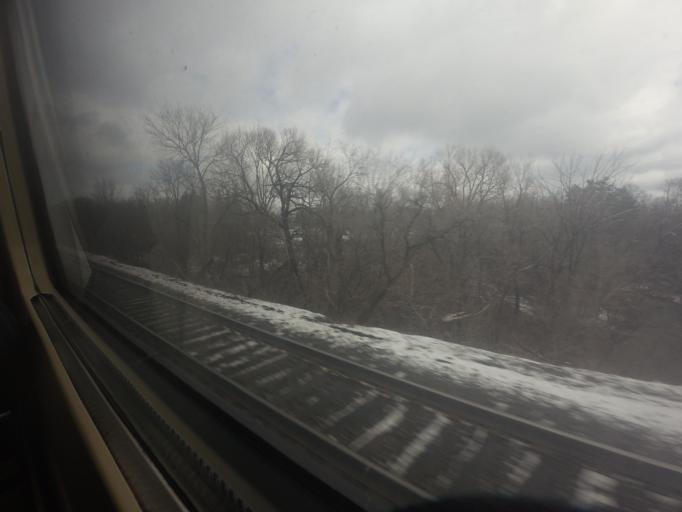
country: CA
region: Ontario
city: Ajax
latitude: 43.8059
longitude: -79.1151
